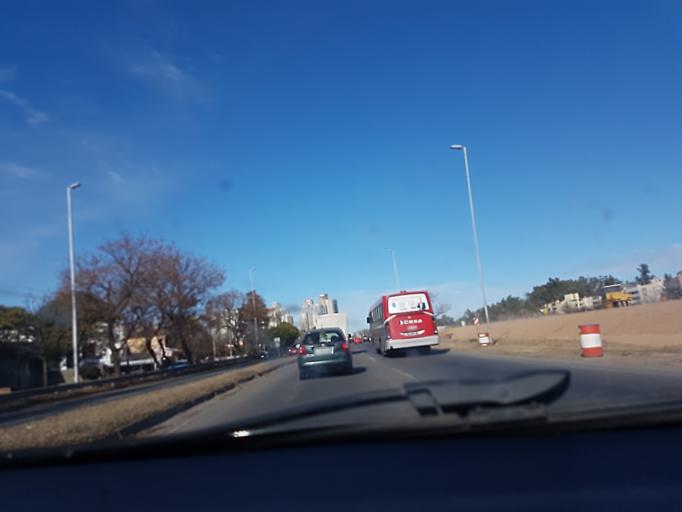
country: AR
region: Cordoba
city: La Calera
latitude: -31.3866
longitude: -64.2618
